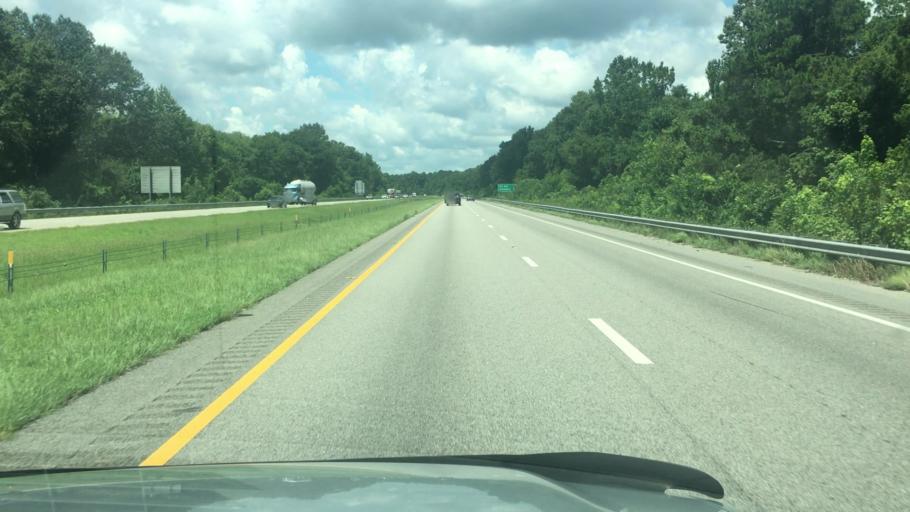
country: US
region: South Carolina
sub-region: Kershaw County
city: Camden
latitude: 34.2190
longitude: -80.6099
